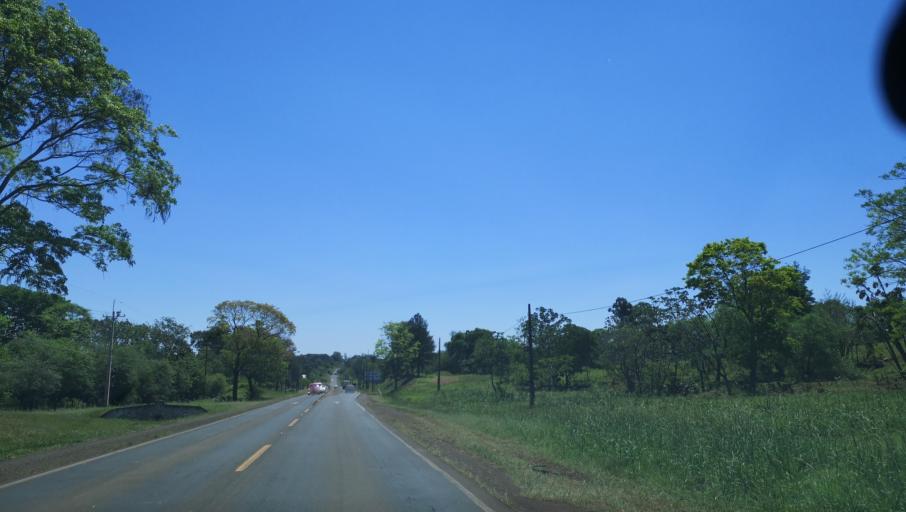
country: PY
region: Itapua
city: San Juan del Parana
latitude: -27.2575
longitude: -55.9828
